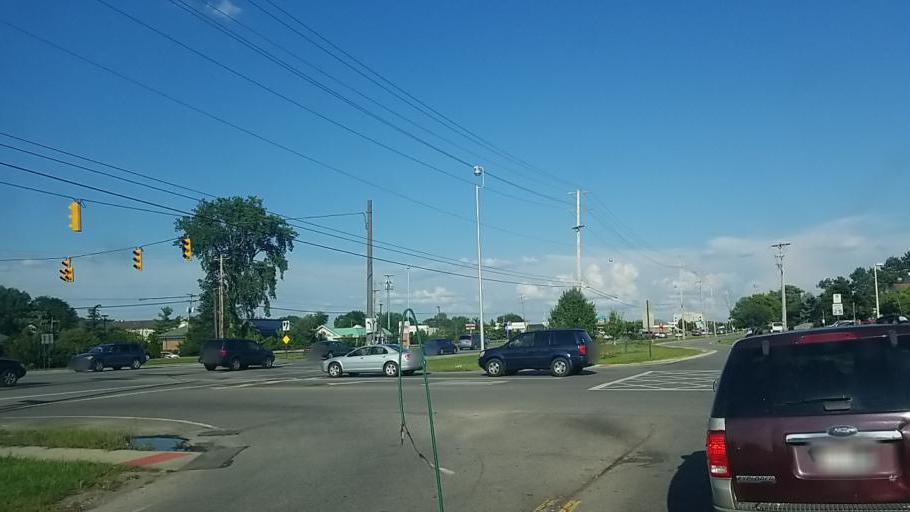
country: US
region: Ohio
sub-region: Franklin County
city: Minerva Park
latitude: 40.0859
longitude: -82.9571
